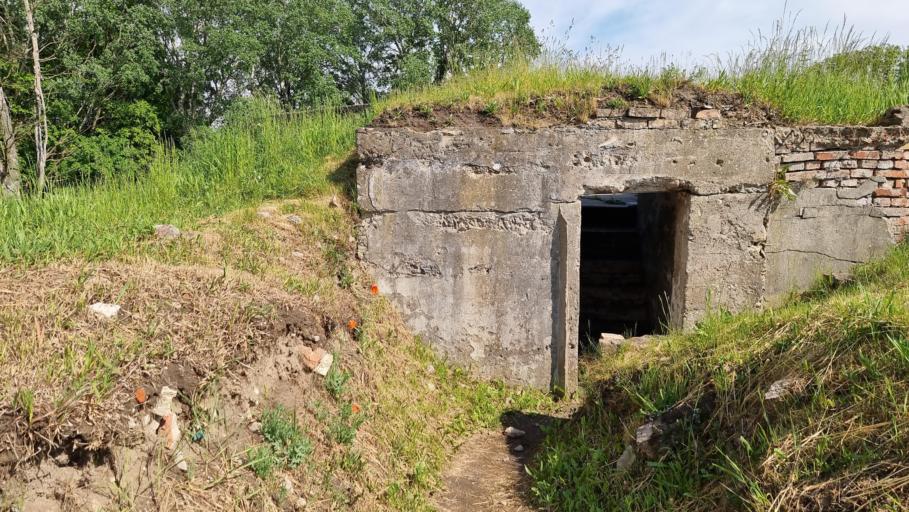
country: PL
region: West Pomeranian Voivodeship
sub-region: Swinoujscie
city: Swinoujscie
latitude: 53.9188
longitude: 14.2758
